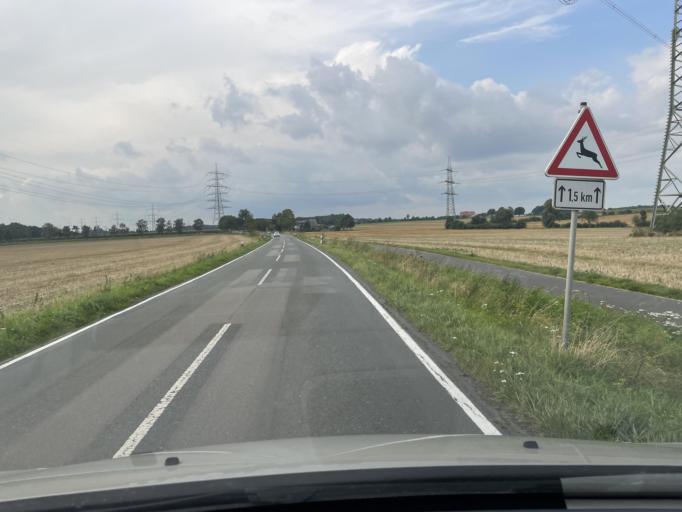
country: DE
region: North Rhine-Westphalia
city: Ahlen
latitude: 51.7521
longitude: 7.8353
